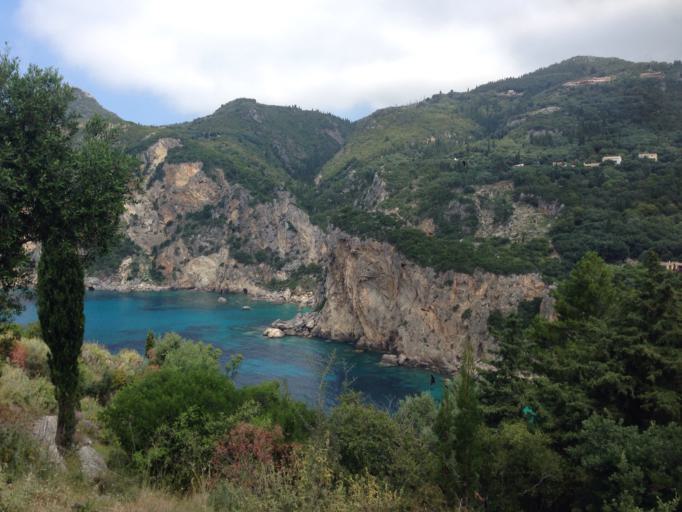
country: GR
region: Ionian Islands
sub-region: Nomos Kerkyras
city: Agios Georgis
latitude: 39.6706
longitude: 19.7002
